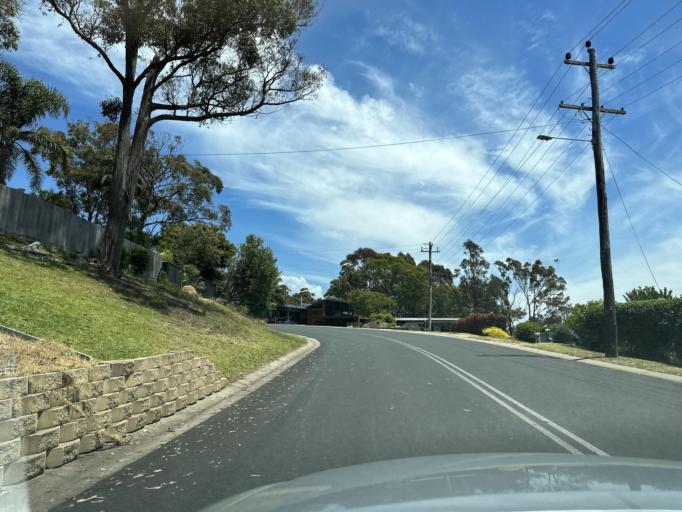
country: AU
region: New South Wales
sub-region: Bega Valley
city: Merimbula
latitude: -36.8909
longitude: 149.9029
